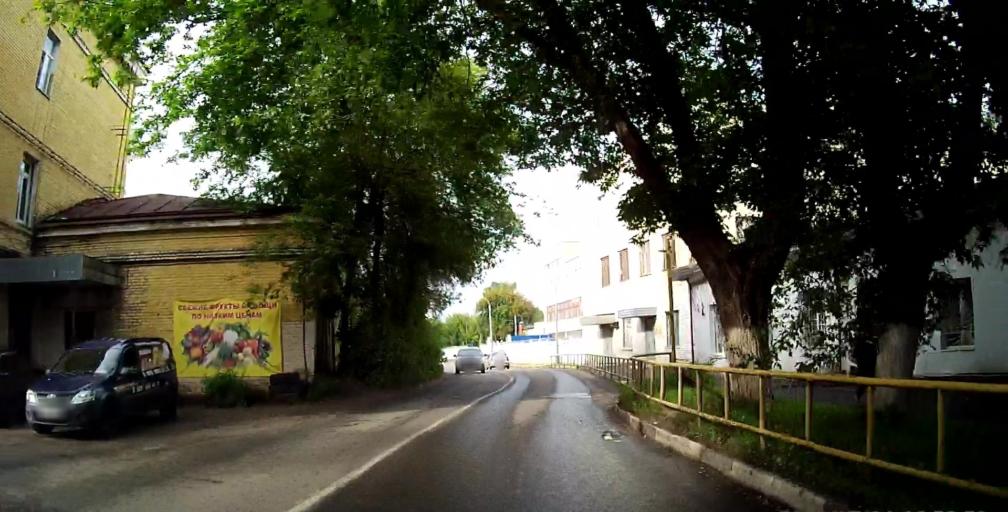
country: RU
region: Moskovskaya
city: Klimovsk
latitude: 55.3792
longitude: 37.5485
